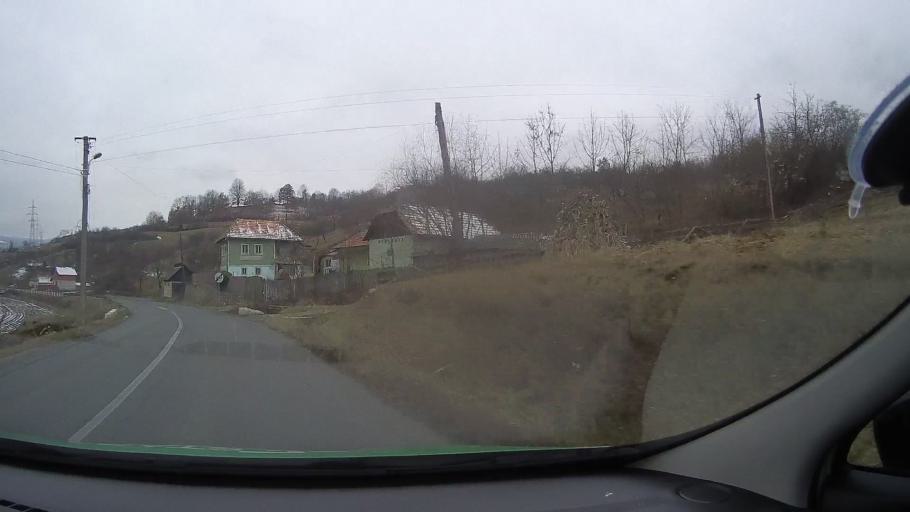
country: RO
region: Alba
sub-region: Comuna Metes
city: Metes
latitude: 46.1035
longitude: 23.4372
